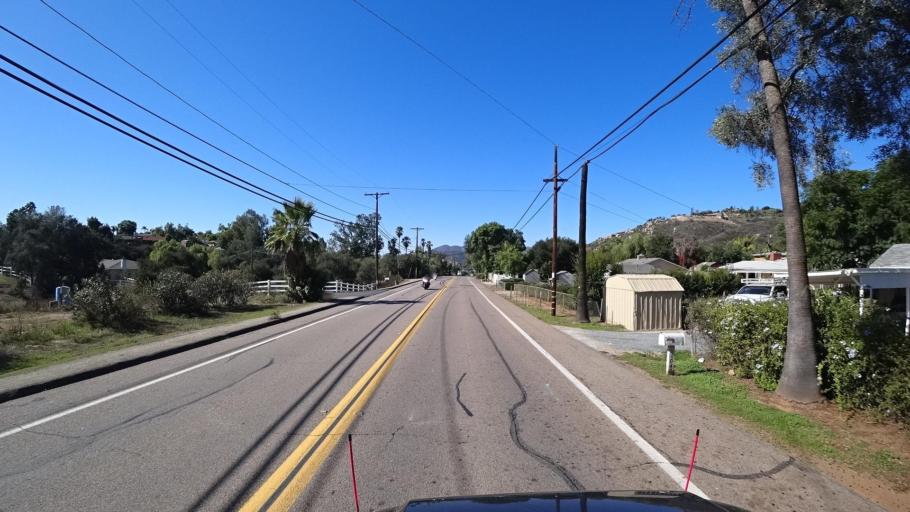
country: US
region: California
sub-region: San Diego County
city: Jamul
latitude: 32.7247
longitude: -116.8711
